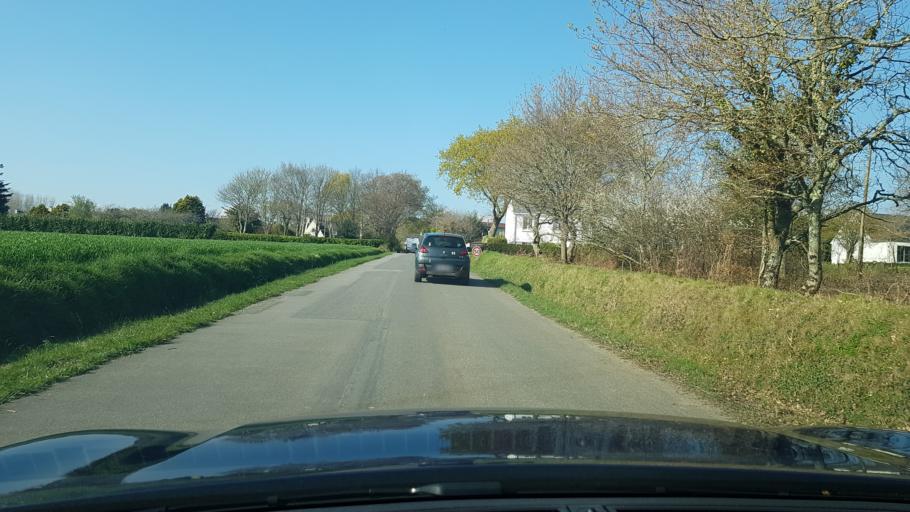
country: FR
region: Brittany
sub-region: Departement du Finistere
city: Moelan-sur-Mer
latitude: 47.7885
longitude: -3.6251
